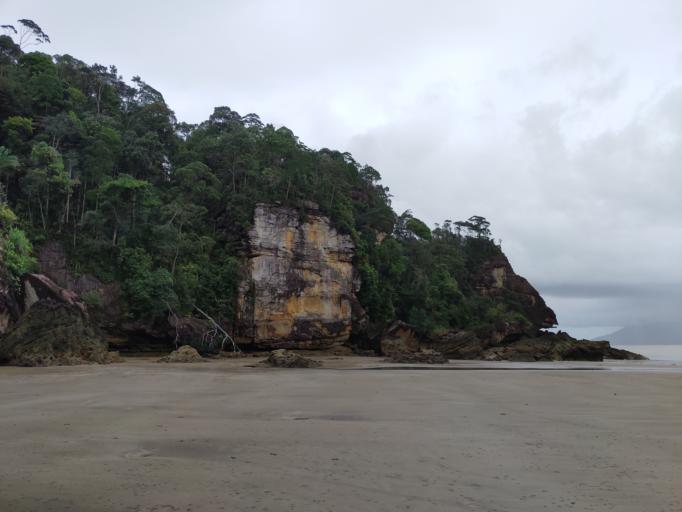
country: MY
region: Sarawak
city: Kuching
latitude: 1.7161
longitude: 110.4415
